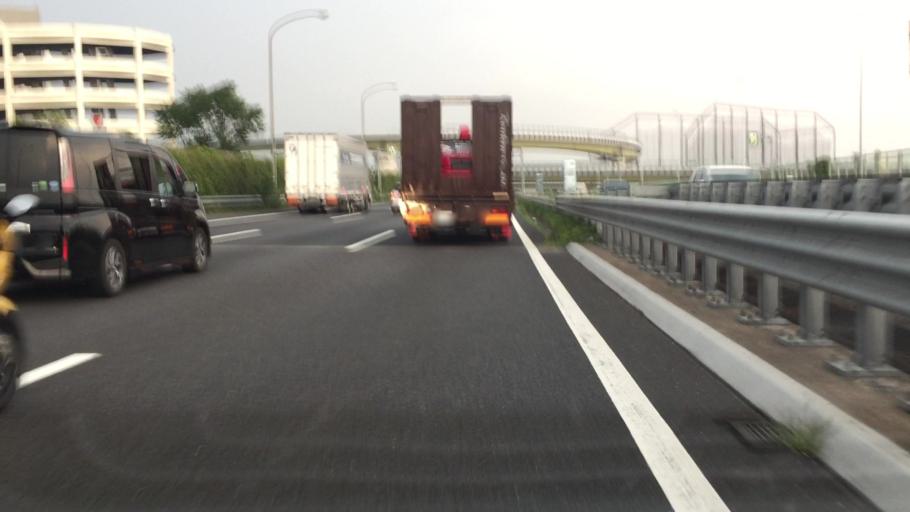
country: JP
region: Saitama
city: Kukichuo
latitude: 36.0522
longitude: 139.6571
